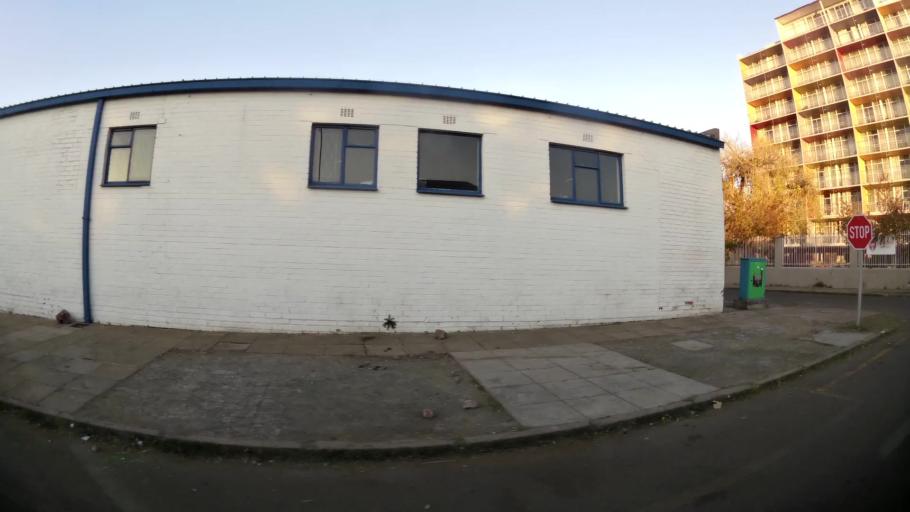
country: ZA
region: Northern Cape
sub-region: Frances Baard District Municipality
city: Kimberley
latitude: -28.7382
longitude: 24.7676
